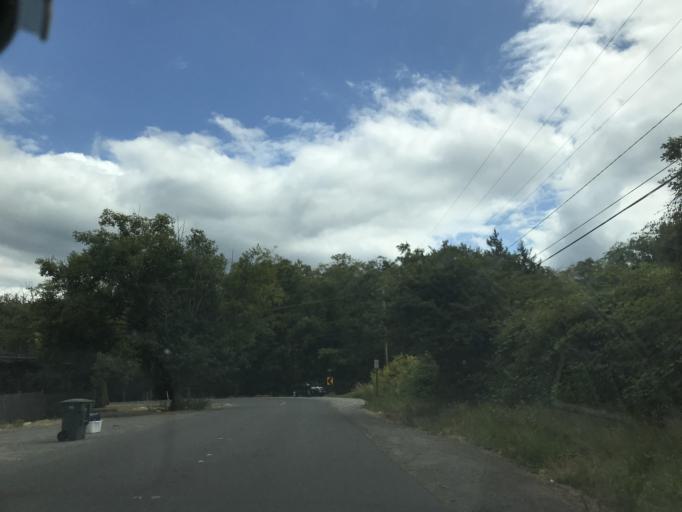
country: US
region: Washington
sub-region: Whatcom County
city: Bellingham
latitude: 48.7240
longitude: -122.4791
